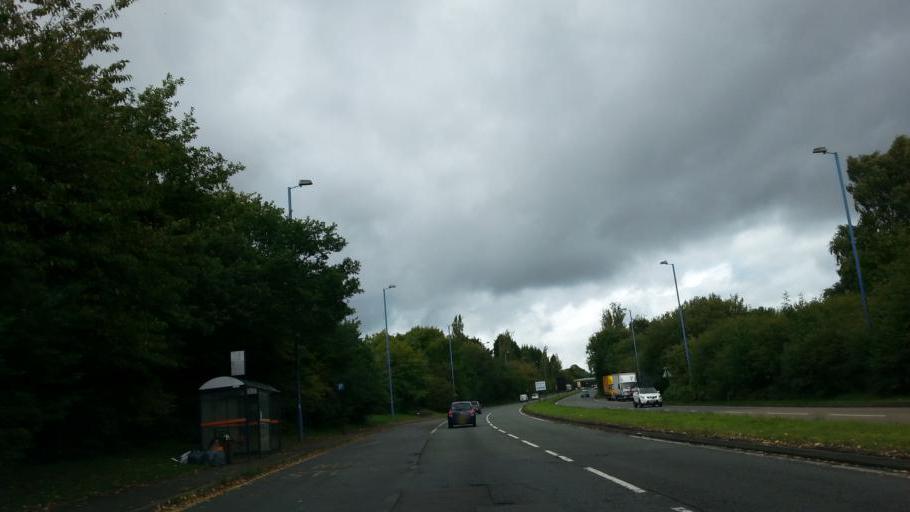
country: GB
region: England
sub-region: City and Borough of Birmingham
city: Bartley Green
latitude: 52.4547
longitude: -2.0086
